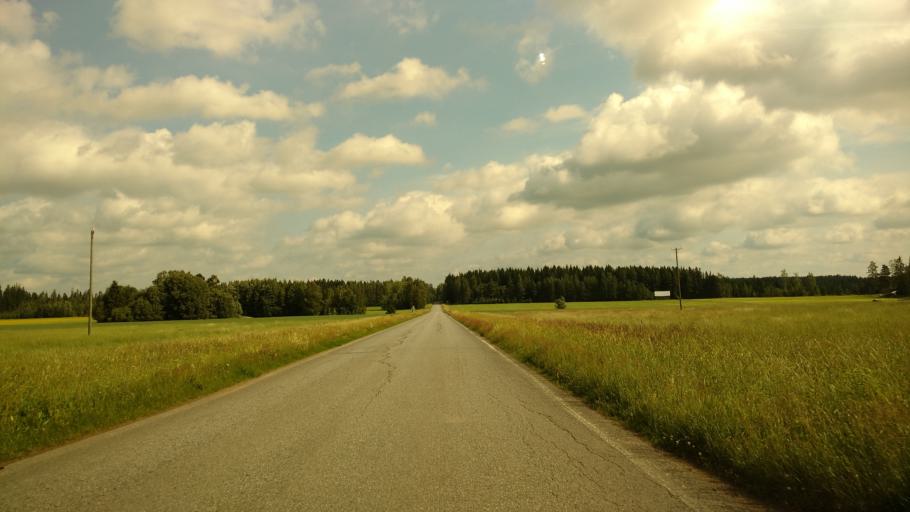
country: FI
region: Haeme
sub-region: Forssa
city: Ypaejae
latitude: 60.7535
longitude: 23.2071
